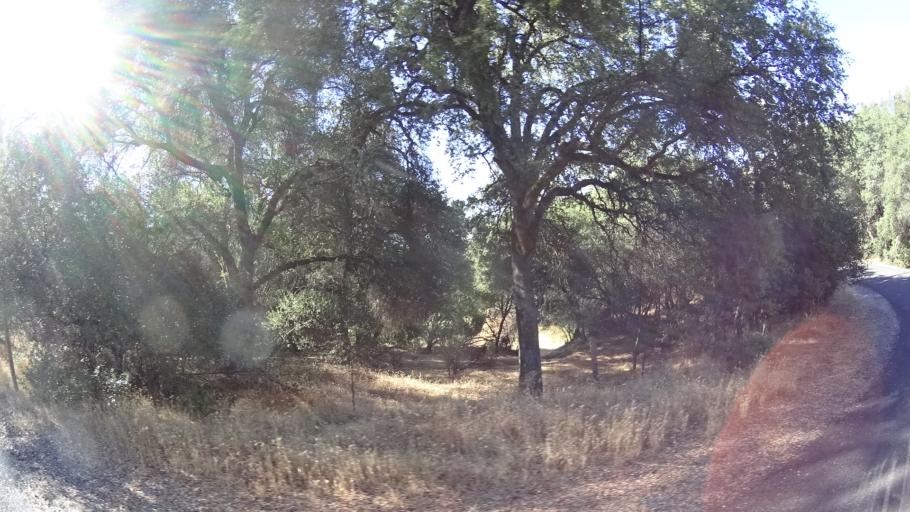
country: US
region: California
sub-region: Calaveras County
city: San Andreas
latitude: 38.2540
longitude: -120.7058
